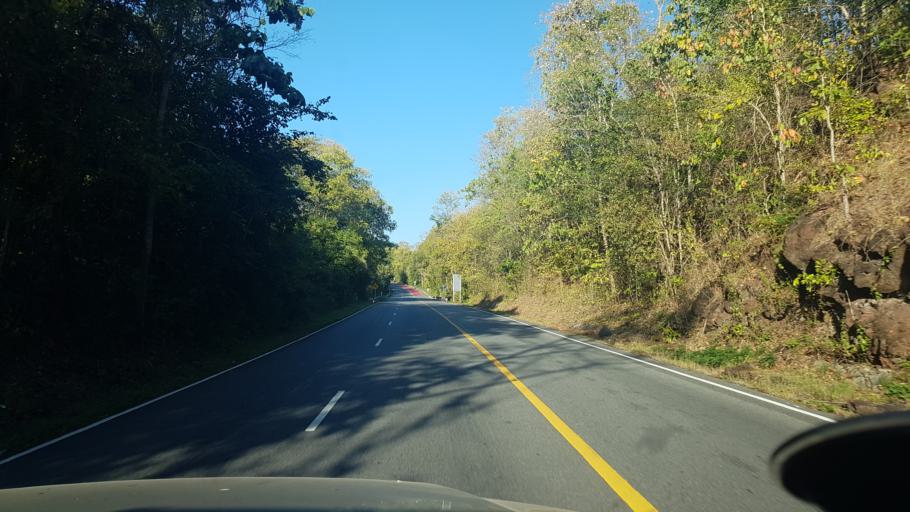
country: TH
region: Phetchabun
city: Nam Nao
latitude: 16.7027
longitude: 101.6606
